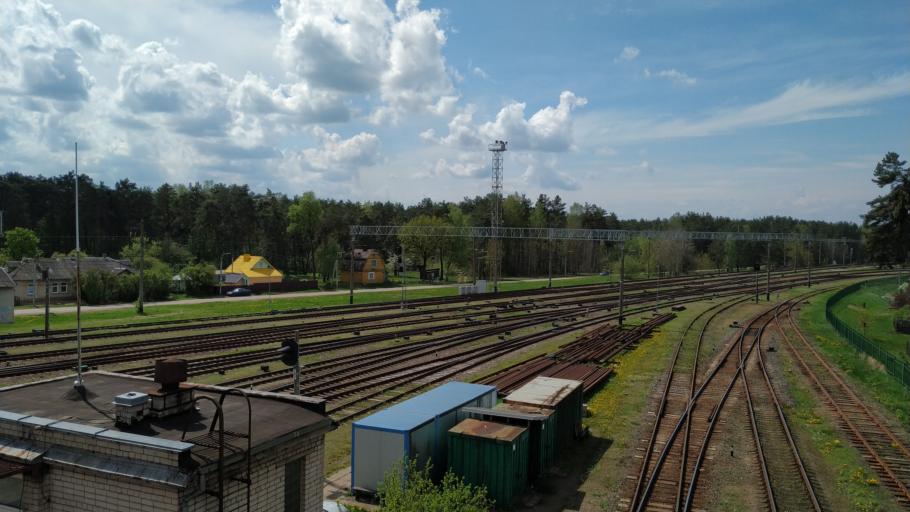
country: LT
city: Baltoji Voke
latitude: 54.6300
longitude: 25.1742
